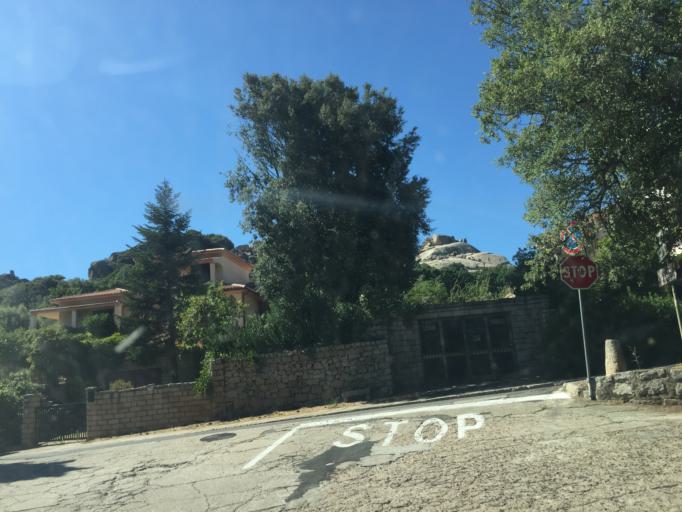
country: IT
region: Sardinia
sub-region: Provincia di Olbia-Tempio
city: Aggius
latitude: 40.9322
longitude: 9.0669
